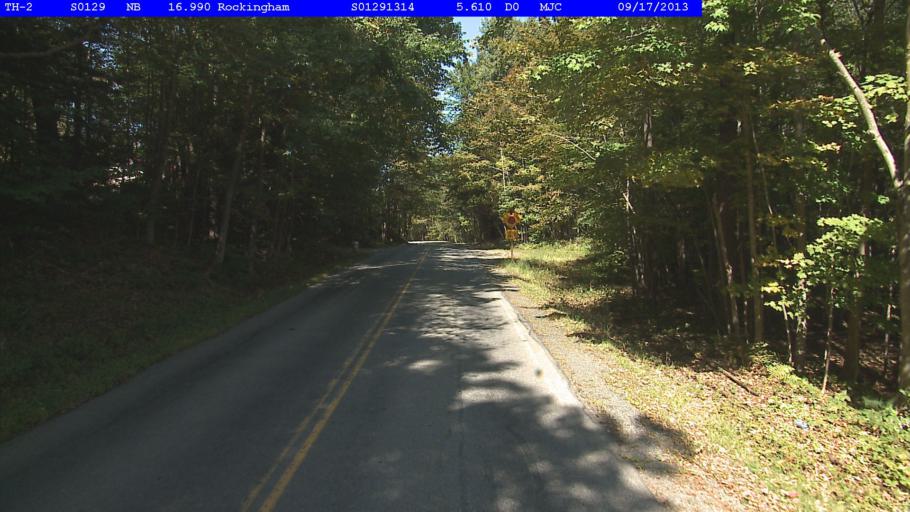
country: US
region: Vermont
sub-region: Windham County
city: Rockingham
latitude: 43.1972
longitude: -72.5118
